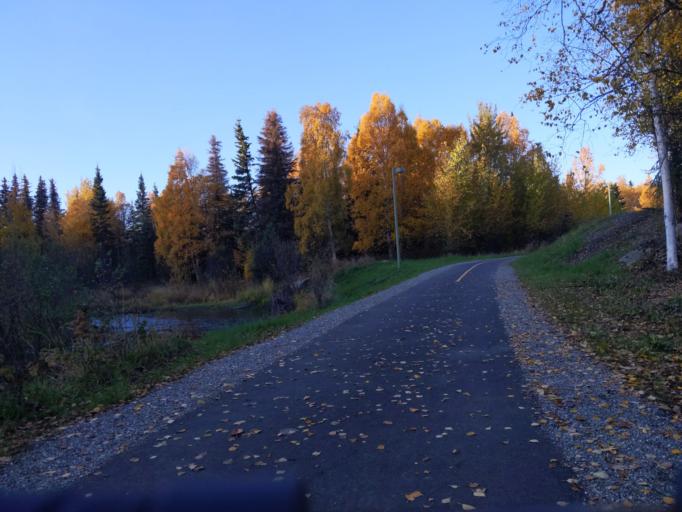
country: US
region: Alaska
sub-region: Anchorage Municipality
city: Anchorage
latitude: 61.1541
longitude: -149.8786
